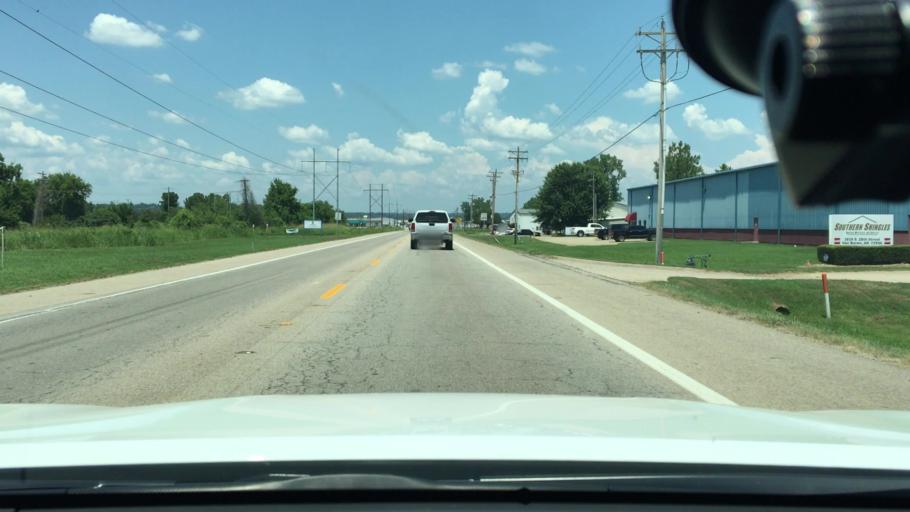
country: US
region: Arkansas
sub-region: Crawford County
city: Van Buren
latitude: 35.4097
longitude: -94.3299
